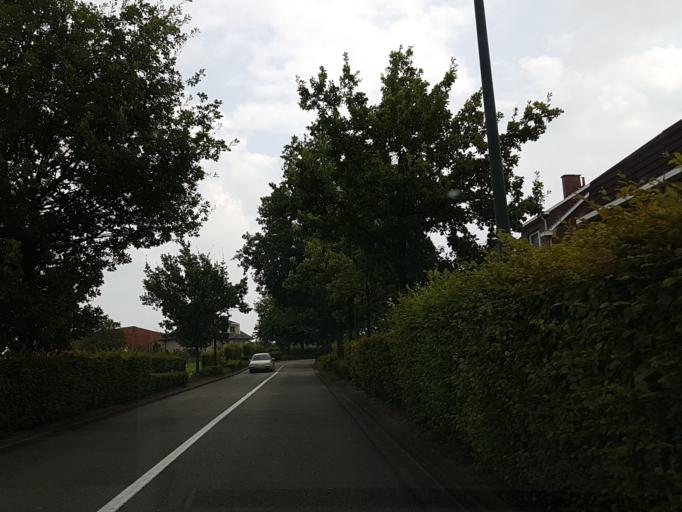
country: BE
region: Flanders
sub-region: Provincie Vlaams-Brabant
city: Zaventem
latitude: 50.8804
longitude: 4.4826
